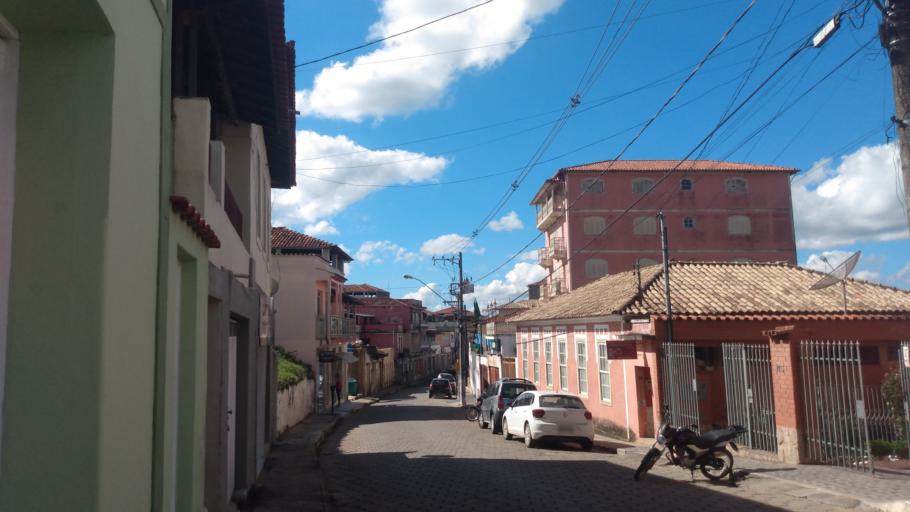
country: BR
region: Minas Gerais
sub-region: Tiradentes
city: Tiradentes
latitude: -20.9233
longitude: -44.2371
